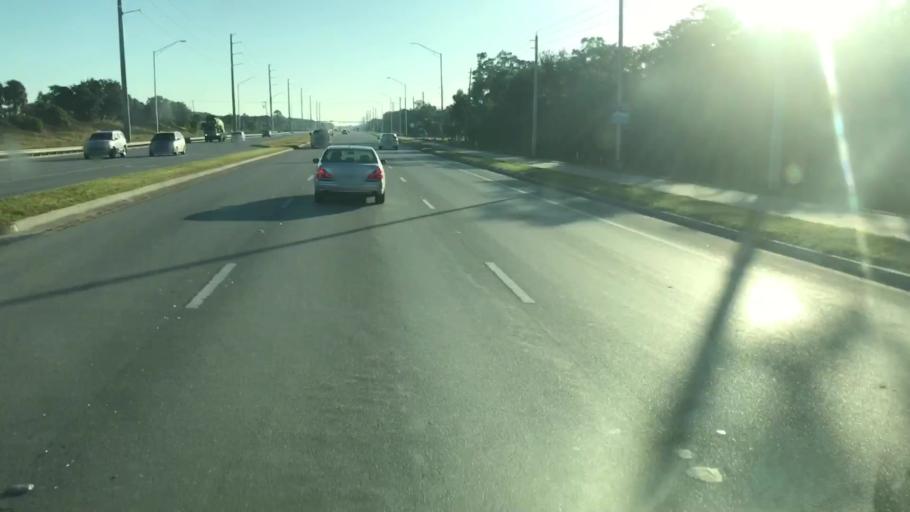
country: US
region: Florida
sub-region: Collier County
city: Orangetree
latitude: 26.2750
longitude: -81.6294
